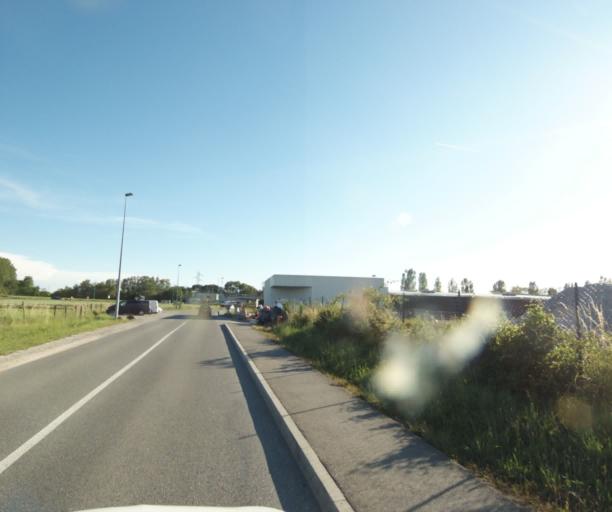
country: FR
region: Rhone-Alpes
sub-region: Departement de la Haute-Savoie
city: Loisin
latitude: 46.2975
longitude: 6.3078
